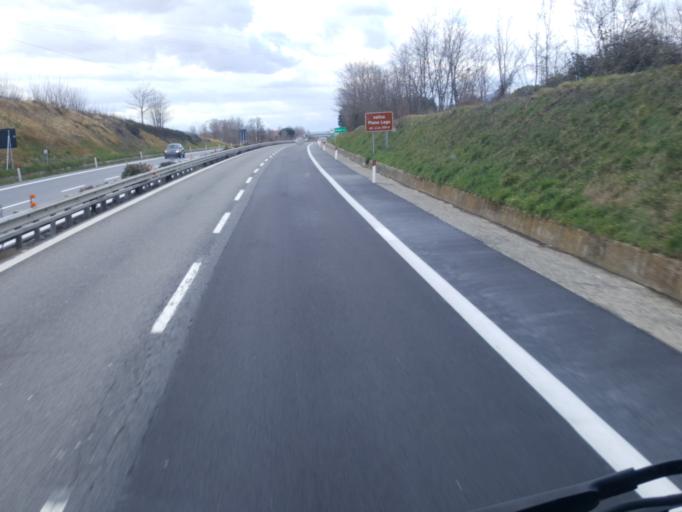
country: IT
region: Calabria
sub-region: Provincia di Cosenza
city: Piane Crati
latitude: 39.2171
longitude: 16.3053
